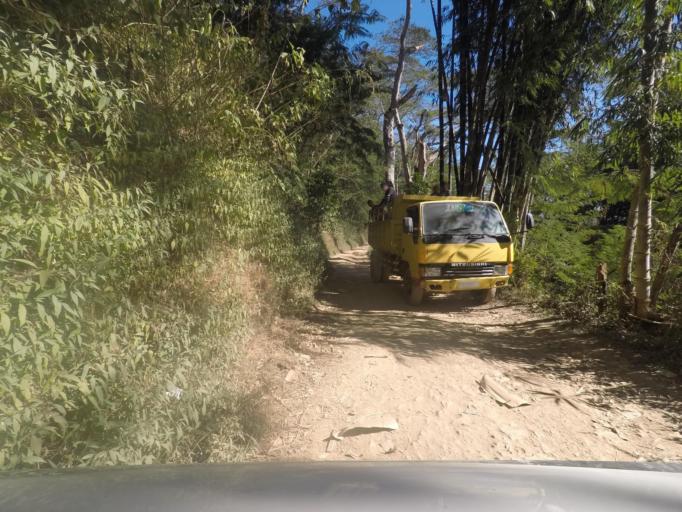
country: TL
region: Ermera
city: Gleno
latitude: -8.7438
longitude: 125.3492
